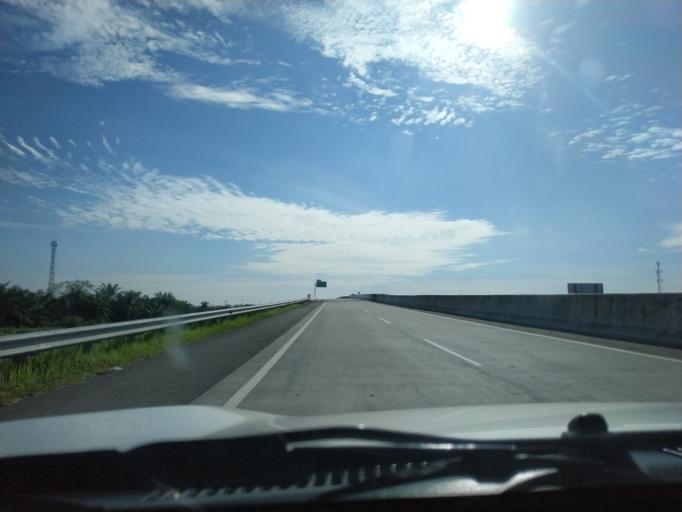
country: ID
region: North Sumatra
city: Perbaungan
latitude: 3.5316
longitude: 98.8841
